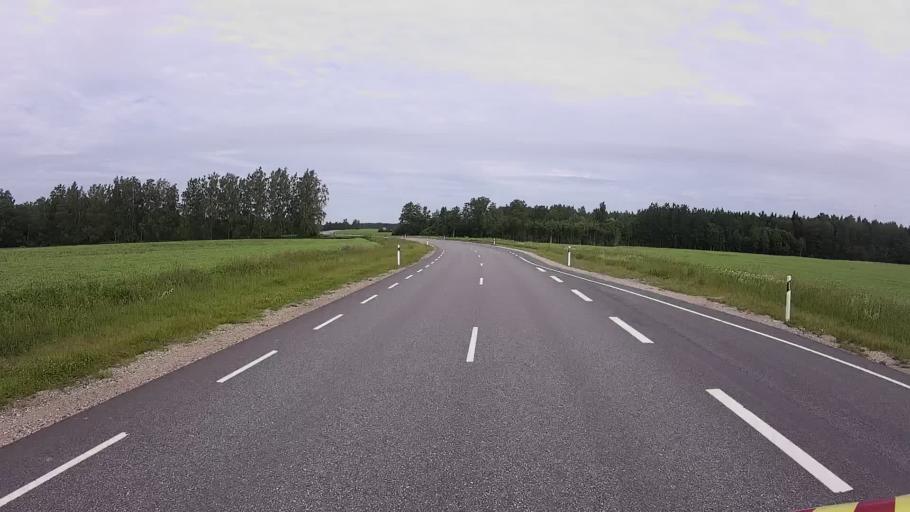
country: EE
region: Viljandimaa
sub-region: Karksi vald
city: Karksi-Nuia
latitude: 58.1577
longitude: 25.5935
